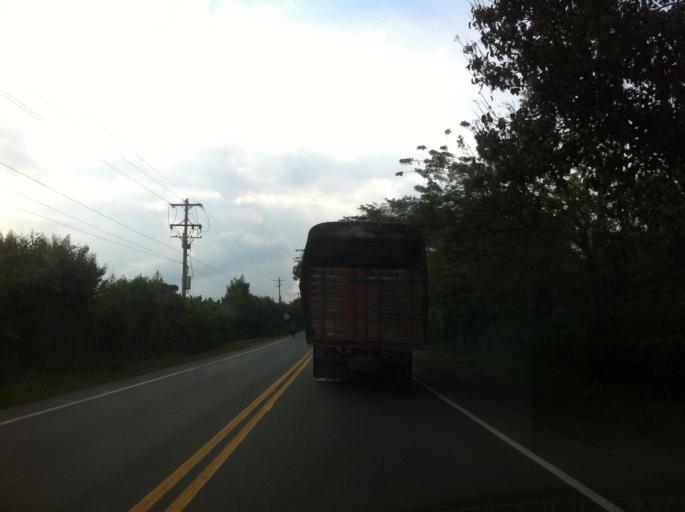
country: CO
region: Quindio
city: La Tebaida
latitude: 4.4479
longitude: -75.8199
